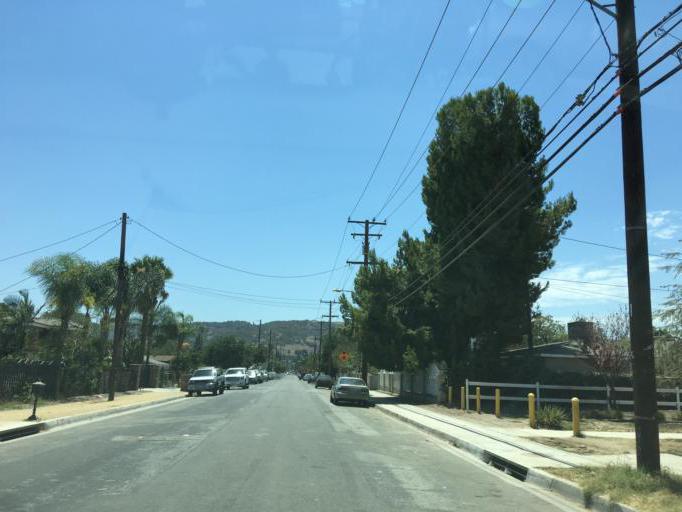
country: US
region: California
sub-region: Los Angeles County
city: Avocado Heights
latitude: 34.0354
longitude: -117.9861
